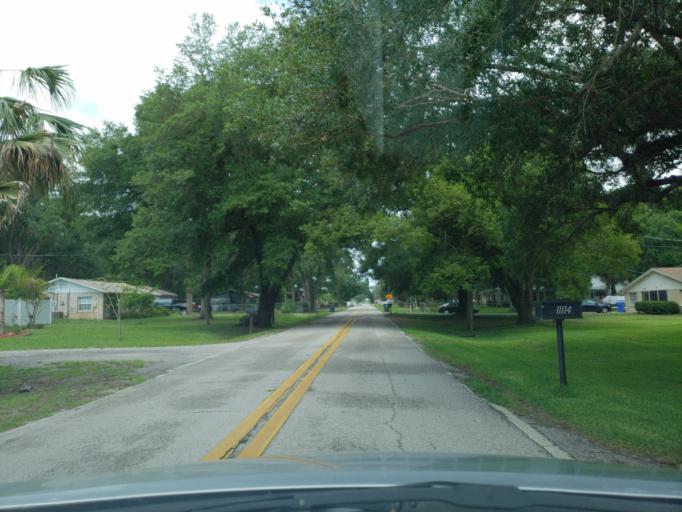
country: US
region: Florida
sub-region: Hillsborough County
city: Riverview
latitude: 27.8717
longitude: -82.3161
